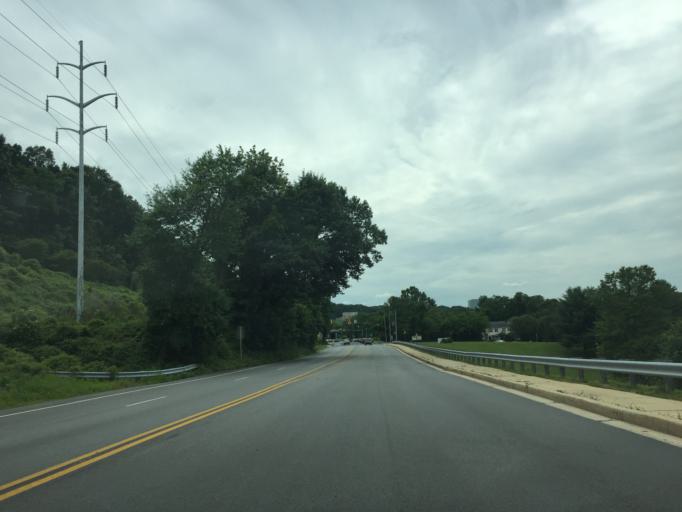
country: US
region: Maryland
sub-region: Baltimore County
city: Hampton
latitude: 39.4038
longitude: -76.5639
